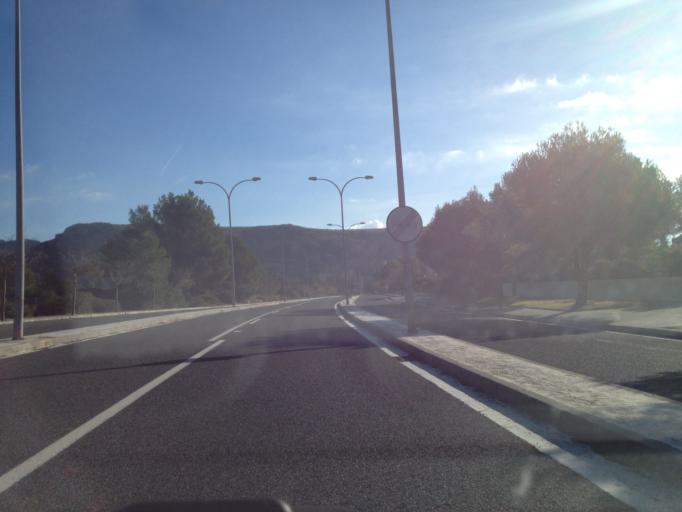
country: ES
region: Balearic Islands
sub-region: Illes Balears
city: Alcudia
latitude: 39.9138
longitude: 3.0952
